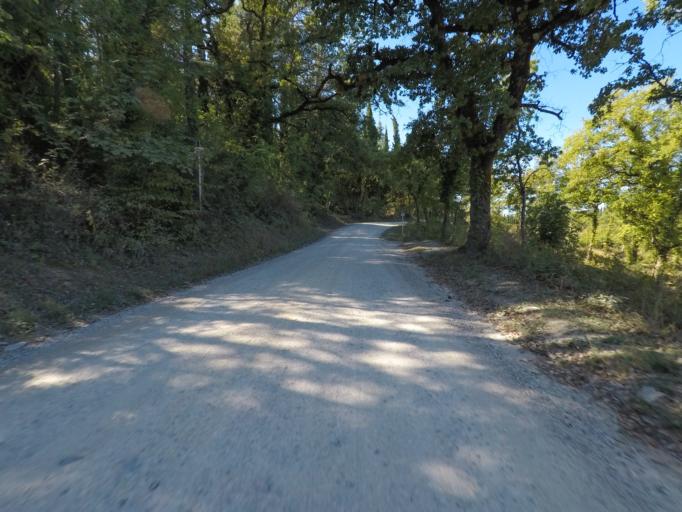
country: IT
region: Tuscany
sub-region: Provincia di Siena
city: Castellina in Chianti
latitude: 43.4357
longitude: 11.3184
